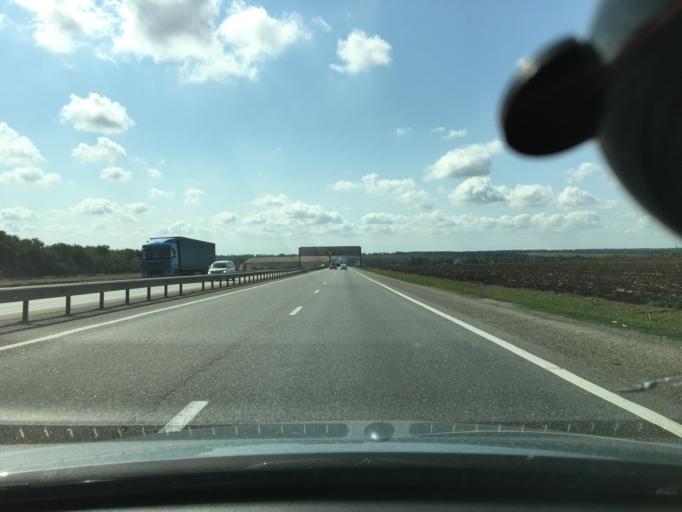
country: RU
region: Krasnodarskiy
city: Krasnoye
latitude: 46.7796
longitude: 39.6646
